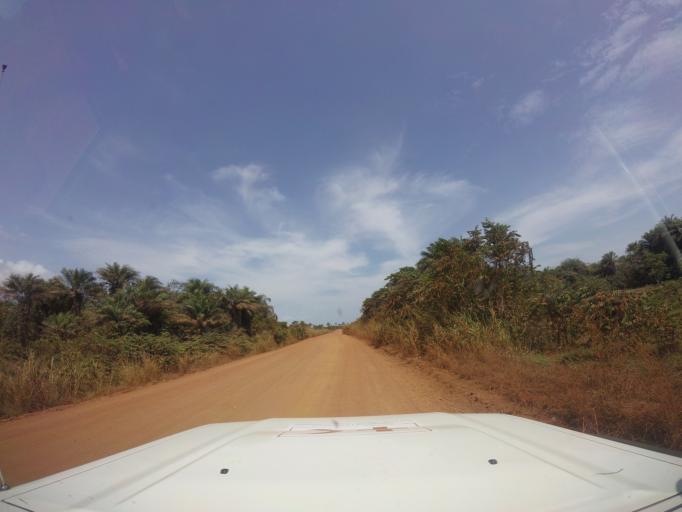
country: LR
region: Grand Cape Mount
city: Robertsport
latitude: 6.7487
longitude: -11.3454
